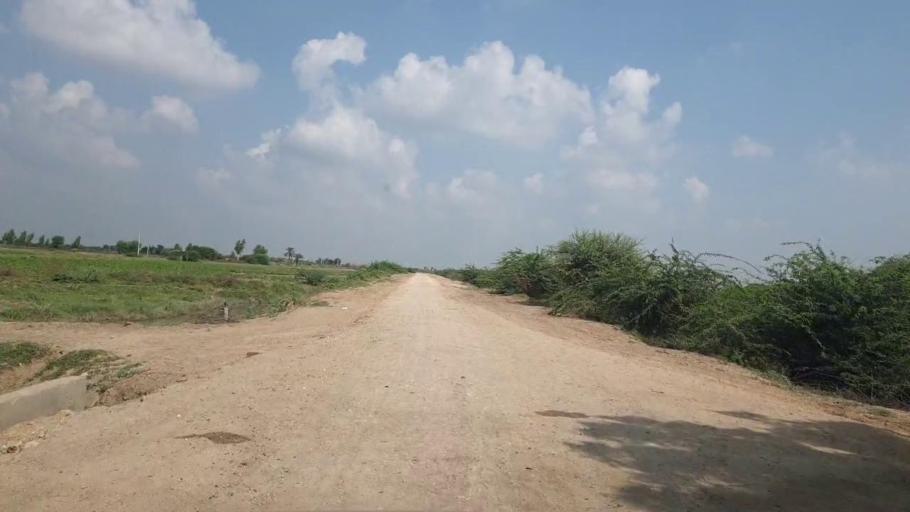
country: PK
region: Sindh
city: Badin
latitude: 24.4800
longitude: 68.6436
